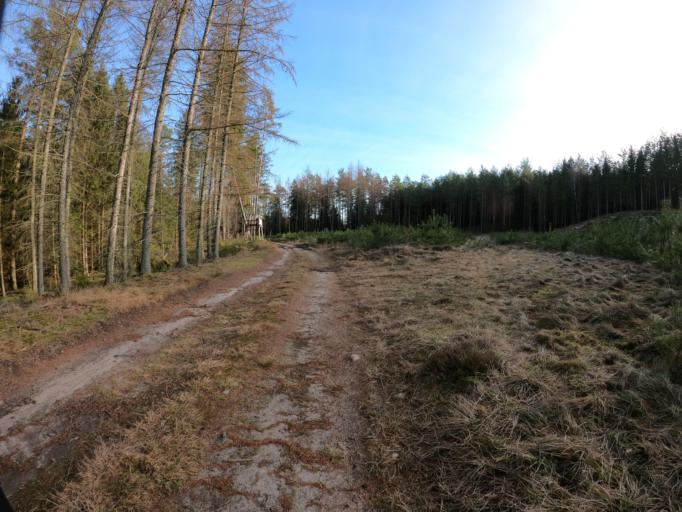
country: PL
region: West Pomeranian Voivodeship
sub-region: Powiat koszalinski
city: Polanow
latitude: 54.1884
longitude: 16.6731
